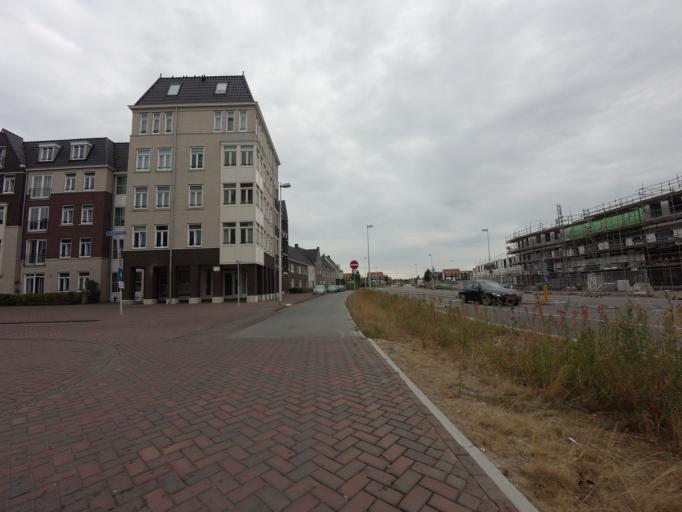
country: NL
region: Utrecht
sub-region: Stichtse Vecht
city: Spechtenkamp
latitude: 52.0922
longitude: 5.0148
